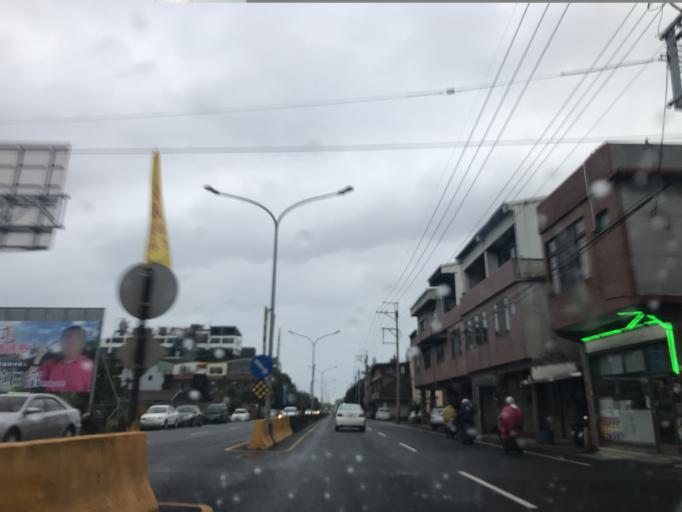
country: TW
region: Taiwan
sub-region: Hsinchu
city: Zhubei
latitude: 24.8246
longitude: 121.0609
